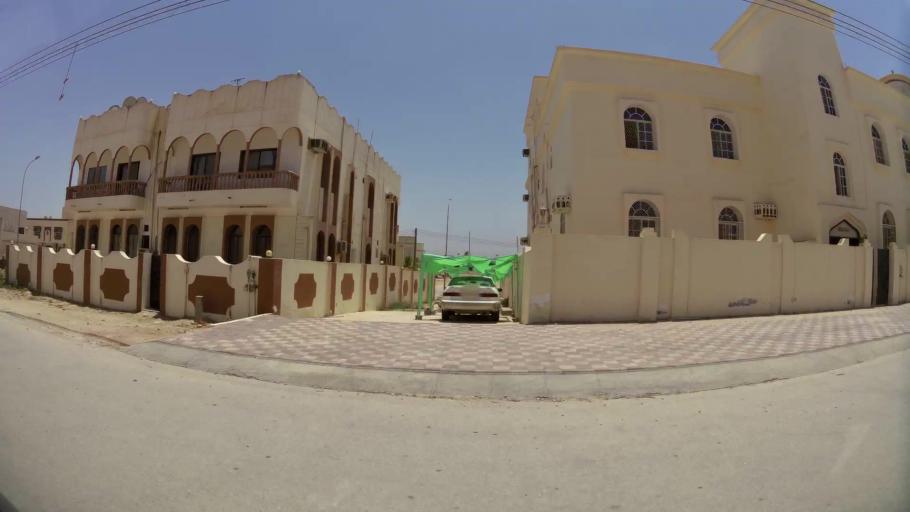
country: OM
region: Zufar
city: Salalah
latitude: 17.0740
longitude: 54.1503
